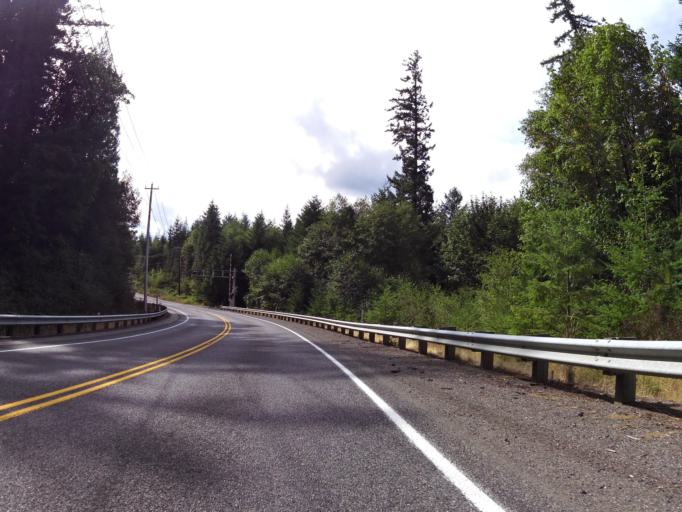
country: US
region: Washington
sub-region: Mason County
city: Shelton
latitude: 47.1468
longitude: -123.0808
